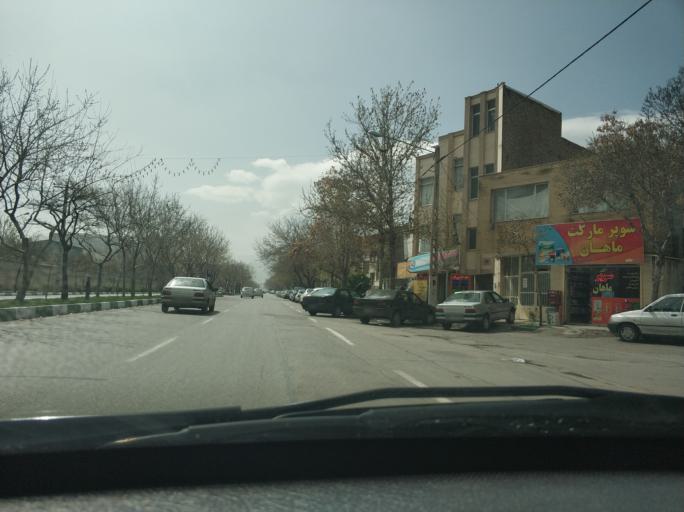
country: IR
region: Razavi Khorasan
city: Mashhad
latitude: 36.2799
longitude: 59.5771
